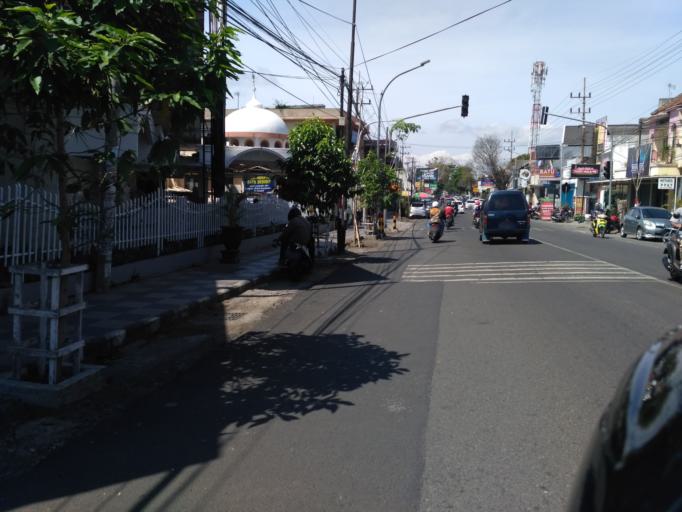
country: ID
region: East Java
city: Batu
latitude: -7.8736
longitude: 112.5295
